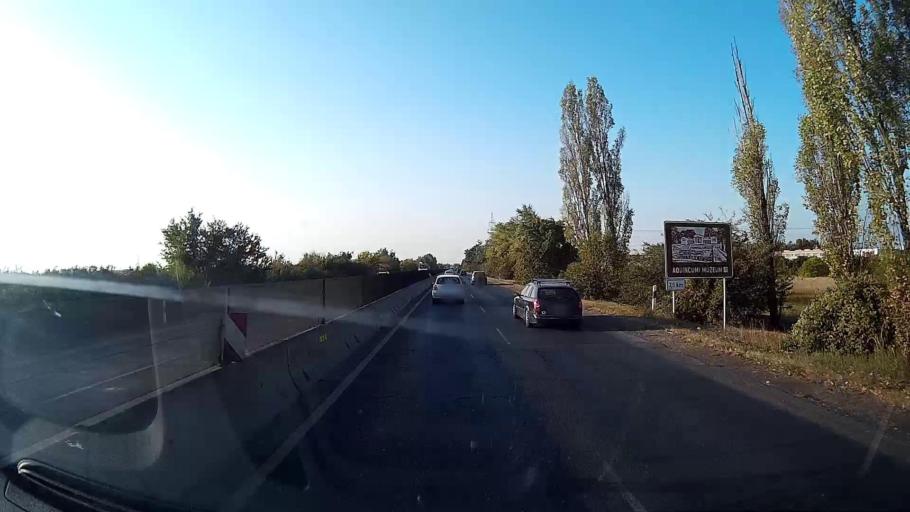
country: HU
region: Pest
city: Budakalasz
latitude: 47.6373
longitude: 19.0720
